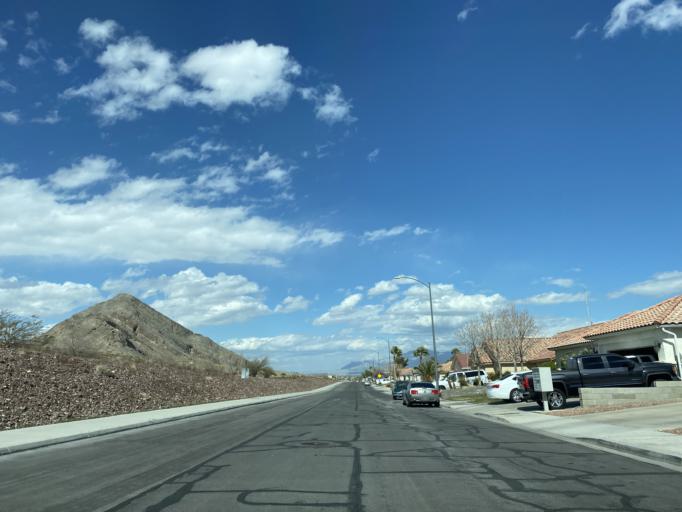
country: US
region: Nevada
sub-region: Clark County
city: Summerlin South
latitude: 36.2266
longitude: -115.3086
